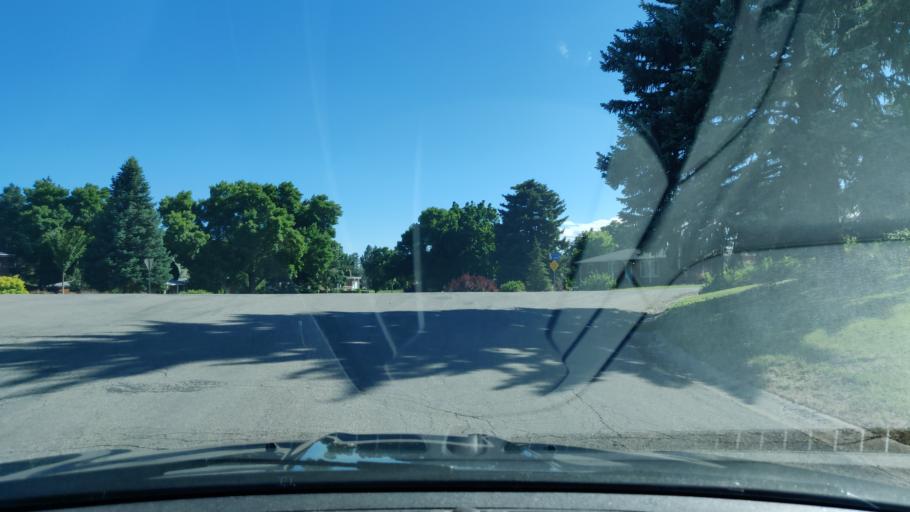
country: US
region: Utah
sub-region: Salt Lake County
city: Cottonwood Heights
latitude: 40.6128
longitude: -111.8127
